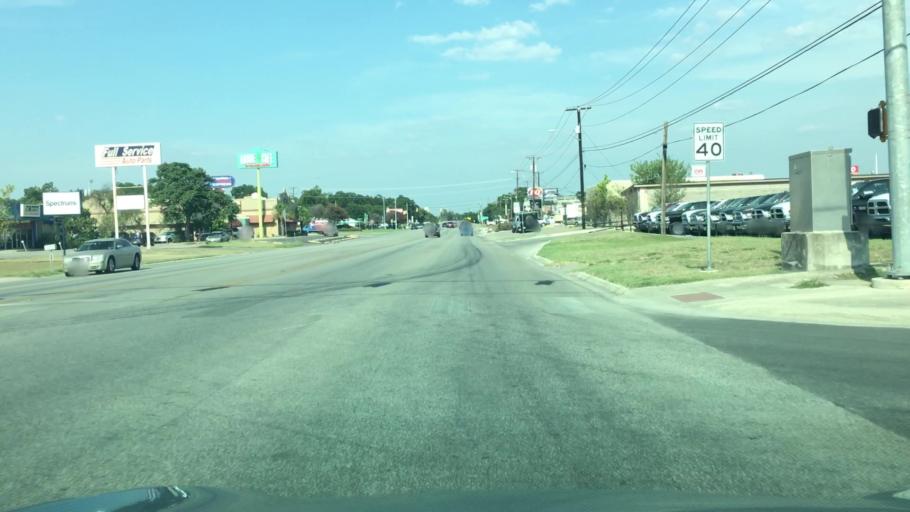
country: US
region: Texas
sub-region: Comal County
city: New Braunfels
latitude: 29.6933
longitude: -98.1144
